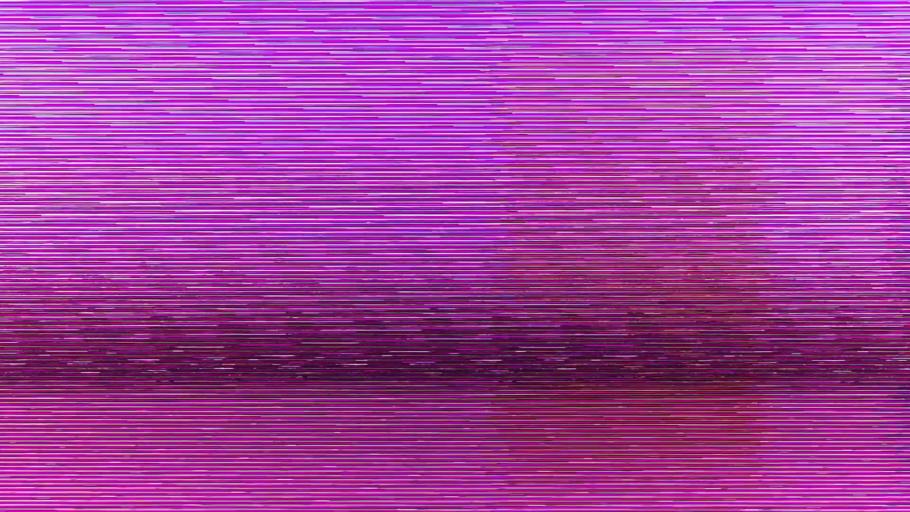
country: US
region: Michigan
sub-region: Oakland County
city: Oxford
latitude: 42.8751
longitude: -83.2995
